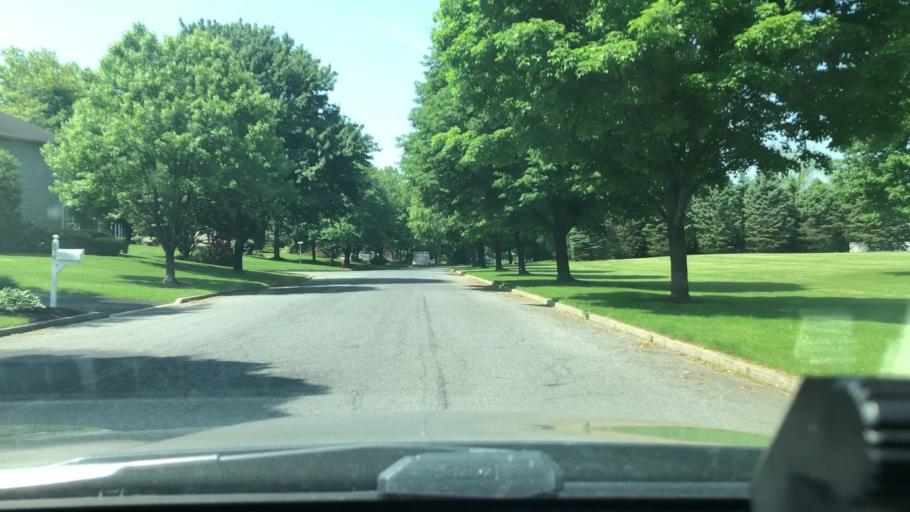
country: US
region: Pennsylvania
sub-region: Northampton County
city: Bethlehem
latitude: 40.6567
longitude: -75.3904
